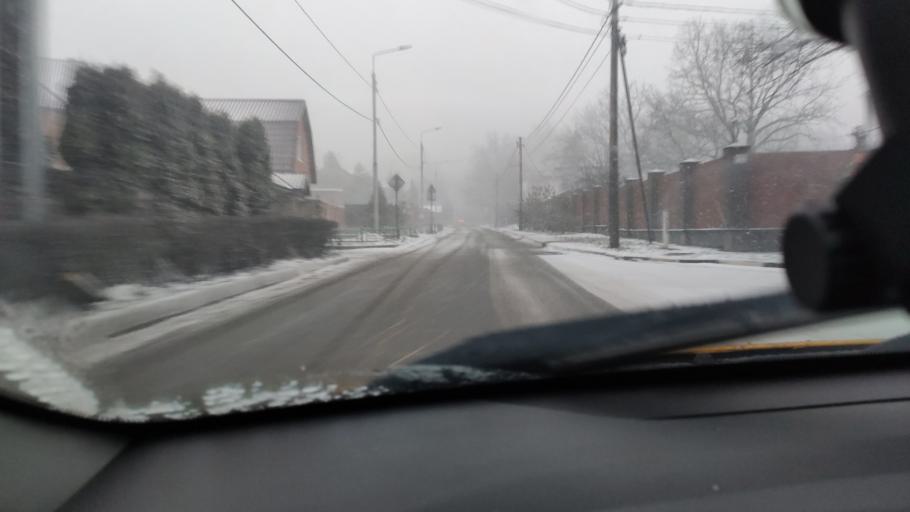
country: RU
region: Moskovskaya
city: Biryulevo Zapadnoye
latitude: 55.5540
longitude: 37.6283
